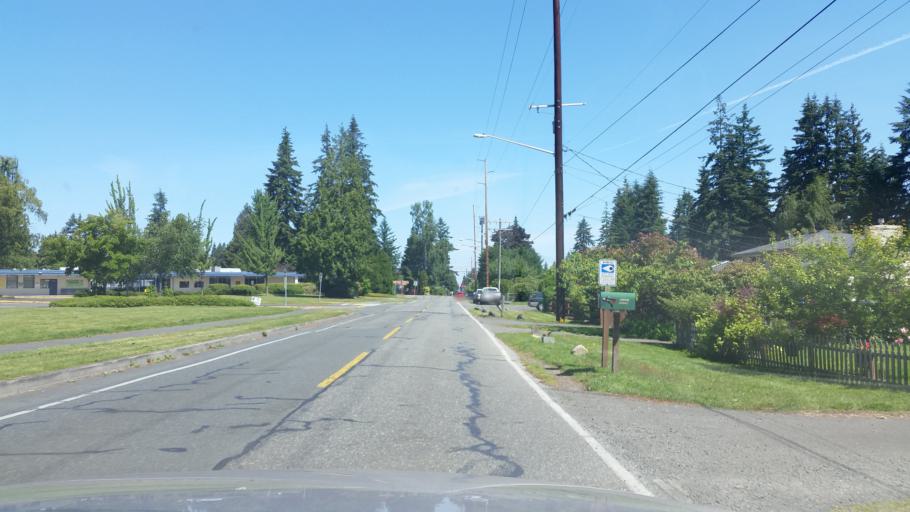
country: US
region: Washington
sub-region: Snohomish County
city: Esperance
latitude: 47.7978
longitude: -122.3616
